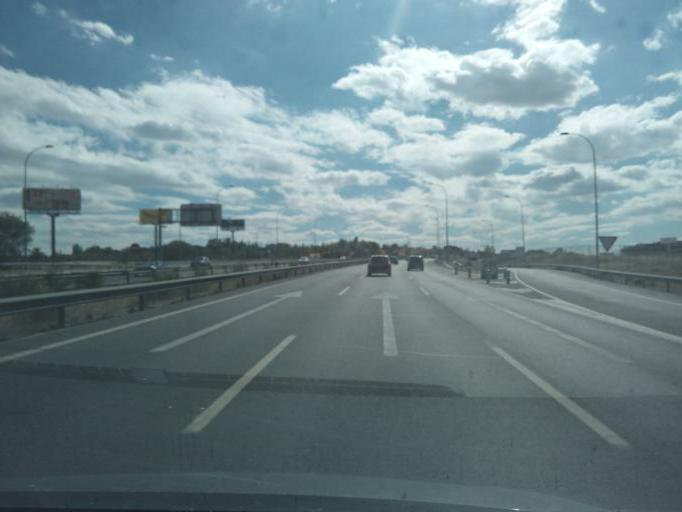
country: ES
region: Madrid
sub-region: Provincia de Madrid
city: San Sebastian de los Reyes
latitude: 40.5350
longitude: -3.6140
